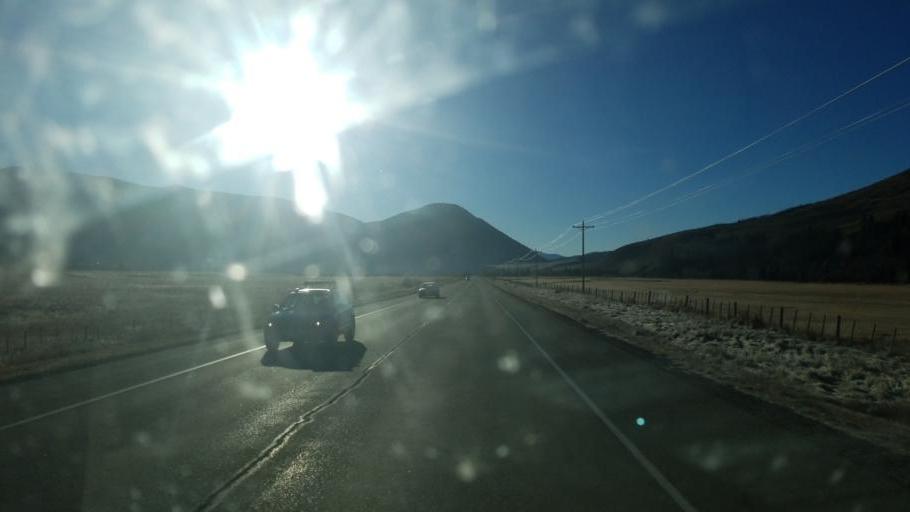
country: US
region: Colorado
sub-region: Gunnison County
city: Crested Butte
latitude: 38.8239
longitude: -106.9169
